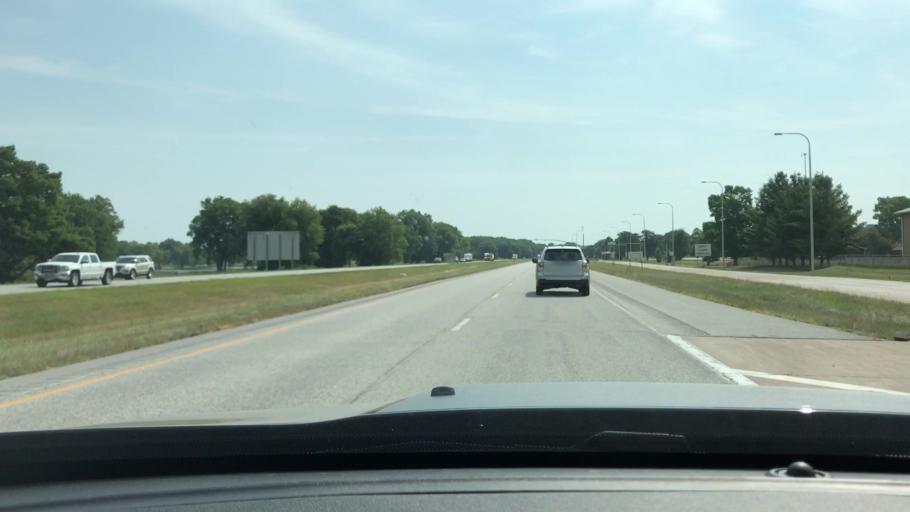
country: US
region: Illinois
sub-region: Rock Island County
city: Coal Valley
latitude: 41.4539
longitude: -90.4747
